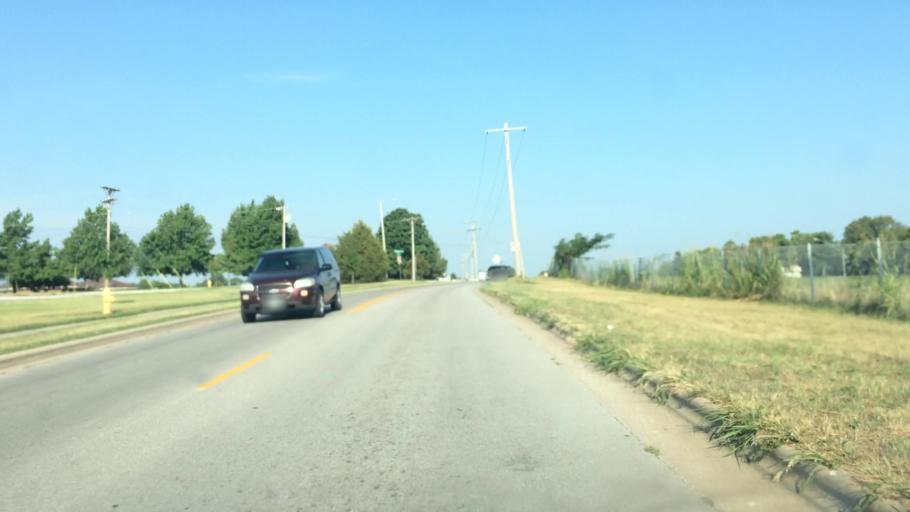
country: US
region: Missouri
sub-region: Greene County
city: Springfield
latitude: 37.2498
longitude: -93.2687
